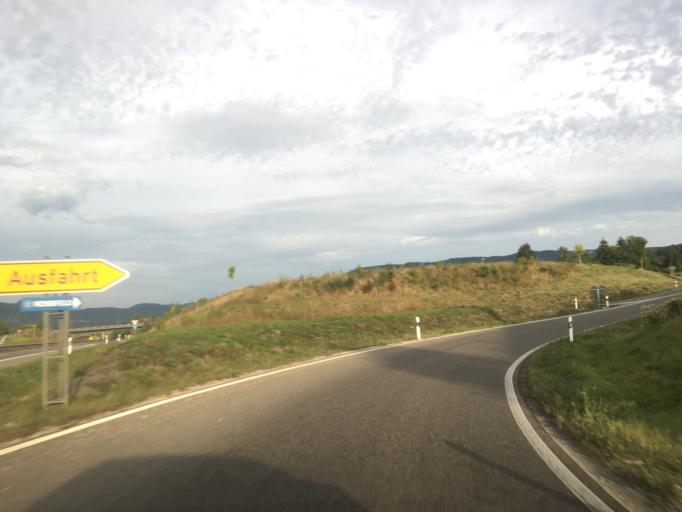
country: DE
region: Baden-Wuerttemberg
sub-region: Tuebingen Region
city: Metzingen
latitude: 48.5292
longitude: 9.2711
